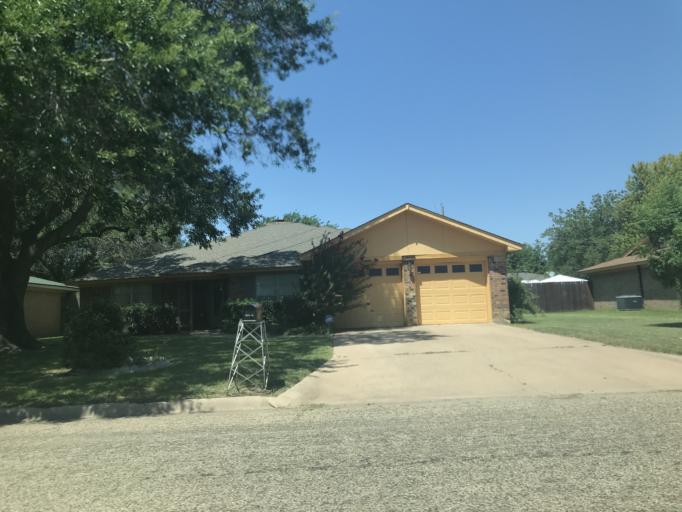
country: US
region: Texas
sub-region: Taylor County
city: Abilene
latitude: 32.4545
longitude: -99.7003
